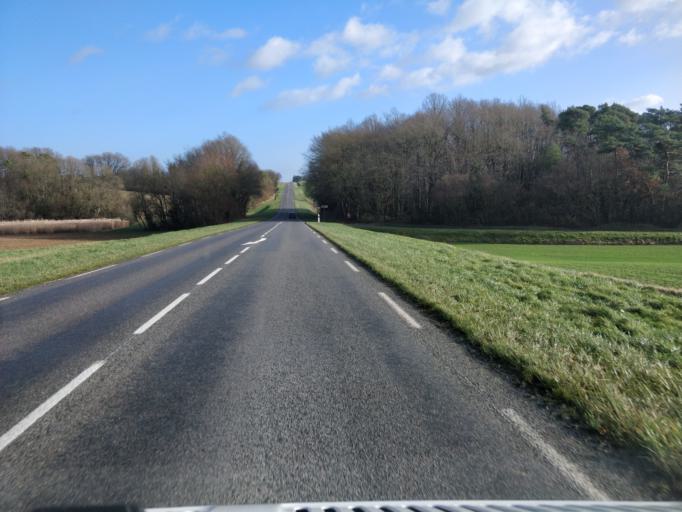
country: FR
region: Ile-de-France
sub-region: Departement de Seine-et-Marne
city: Lorrez-le-Bocage-Preaux
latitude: 48.2206
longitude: 2.8634
